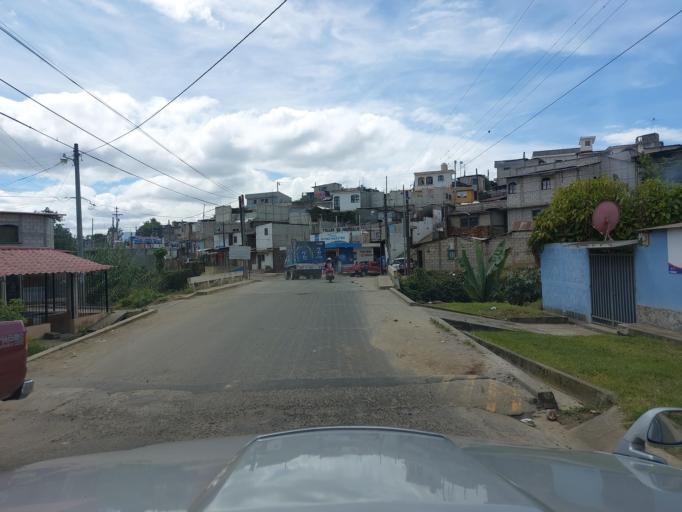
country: GT
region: Chimaltenango
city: San Andres Itzapa
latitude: 14.6205
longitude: -90.8364
